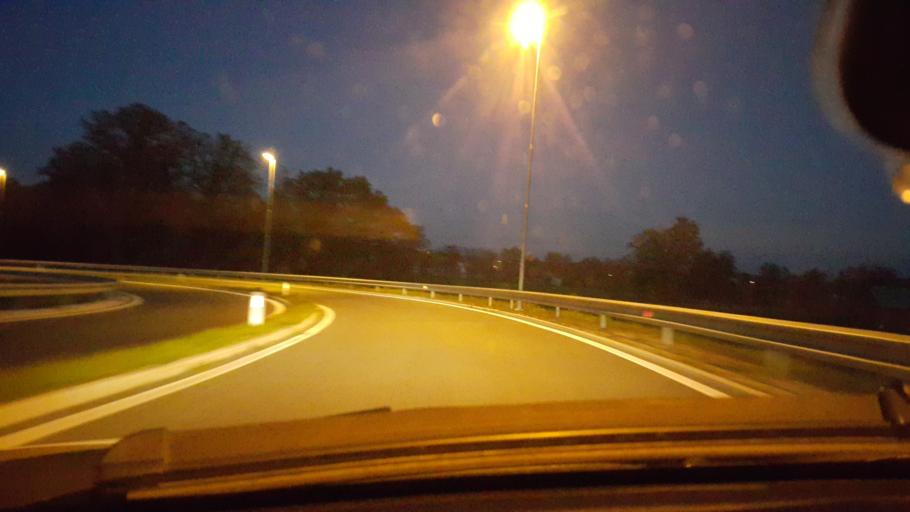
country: SI
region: Celje
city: Ljubecna
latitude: 46.2531
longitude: 15.3112
